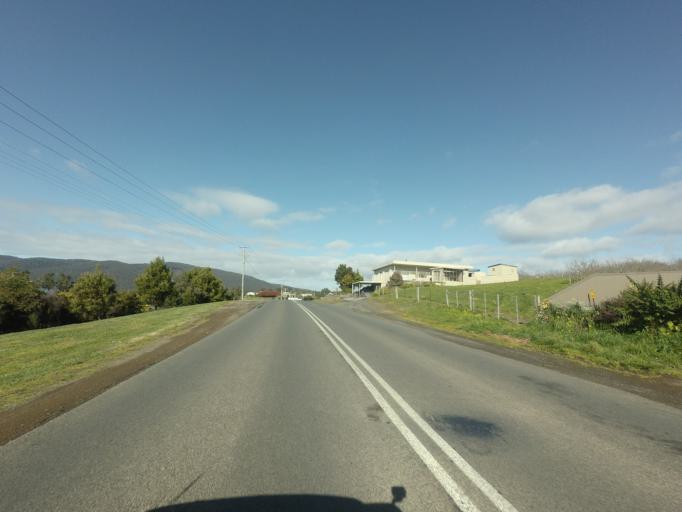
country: AU
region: Tasmania
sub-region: Huon Valley
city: Geeveston
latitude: -43.3188
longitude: 147.0091
